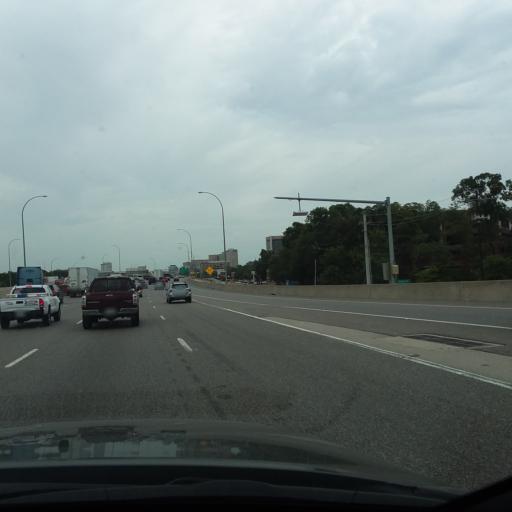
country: US
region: Texas
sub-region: Dallas County
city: Addison
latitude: 32.9247
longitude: -96.7894
